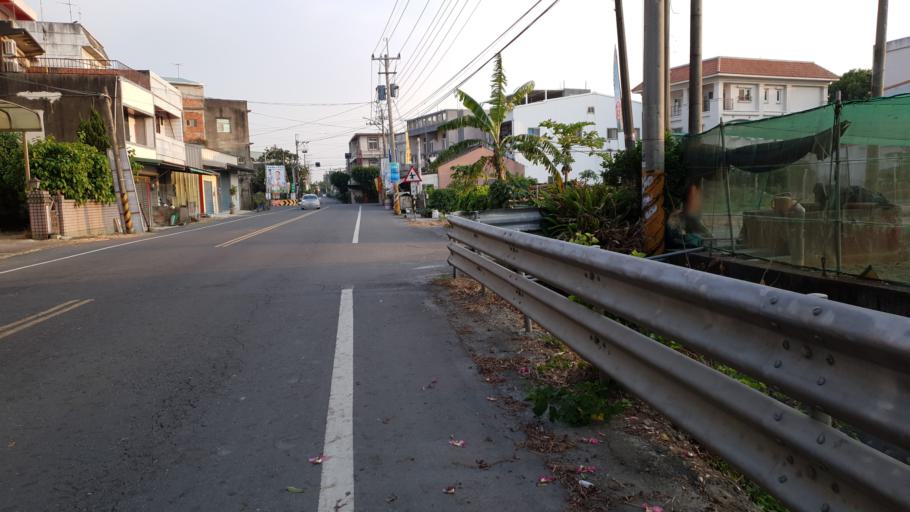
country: TW
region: Taiwan
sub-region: Yunlin
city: Douliu
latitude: 23.7580
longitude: 120.4192
